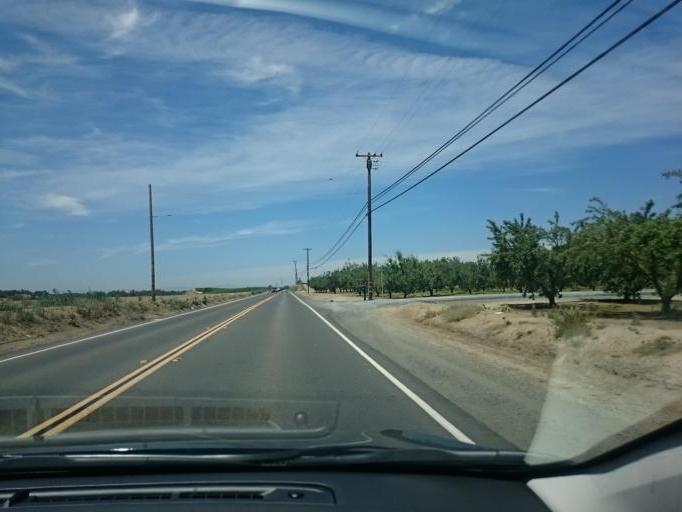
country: US
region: California
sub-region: Stanislaus County
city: Waterford
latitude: 37.6429
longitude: -120.7114
